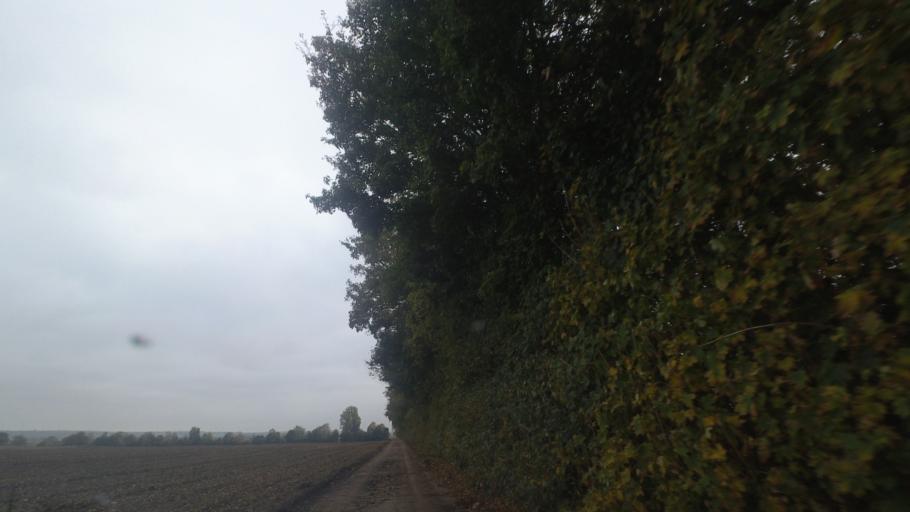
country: DE
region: Rheinland-Pfalz
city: Undenheim
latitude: 49.8323
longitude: 8.2098
